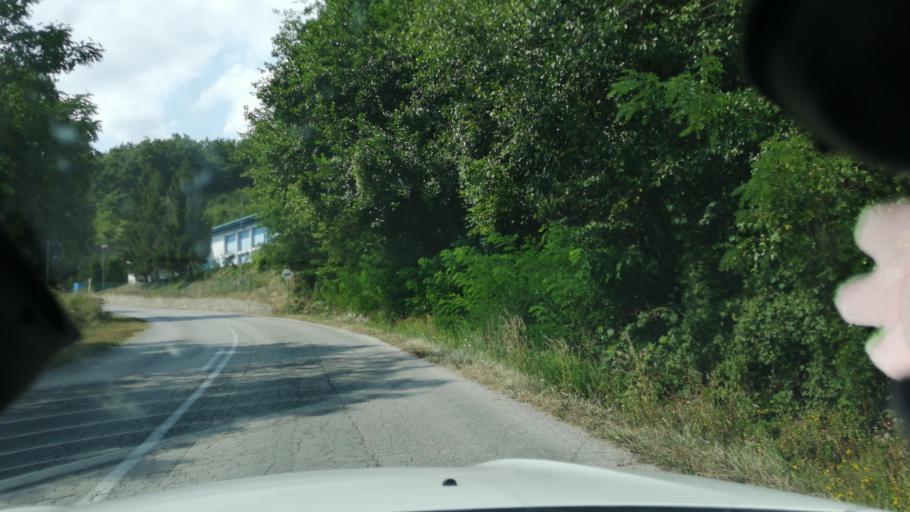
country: RS
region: Central Serbia
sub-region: Moravicki Okrug
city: Ivanjica
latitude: 43.6663
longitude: 20.2545
